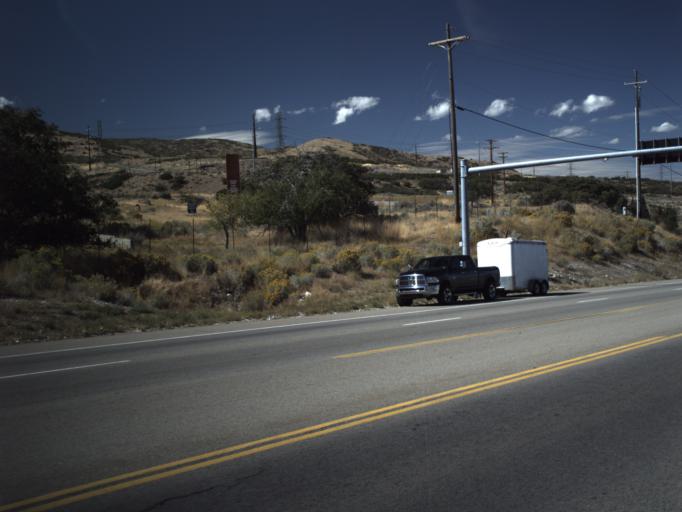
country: US
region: Utah
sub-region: Salt Lake County
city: Bluffdale
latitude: 40.4351
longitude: -111.9299
